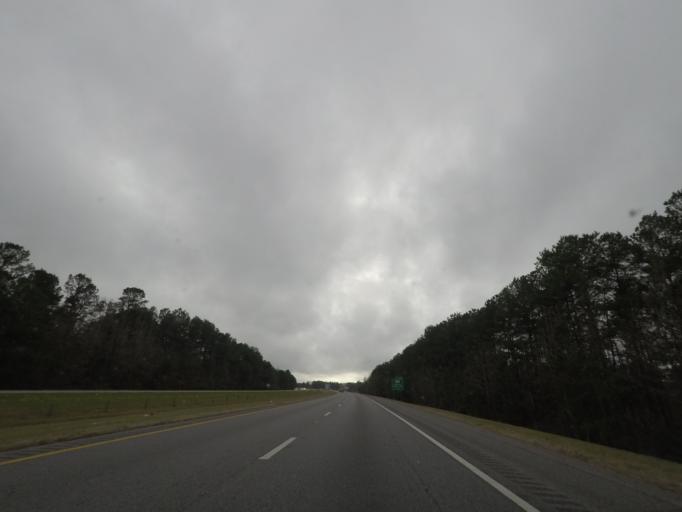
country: US
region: South Carolina
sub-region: Orangeburg County
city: Holly Hill
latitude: 33.4017
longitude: -80.5101
